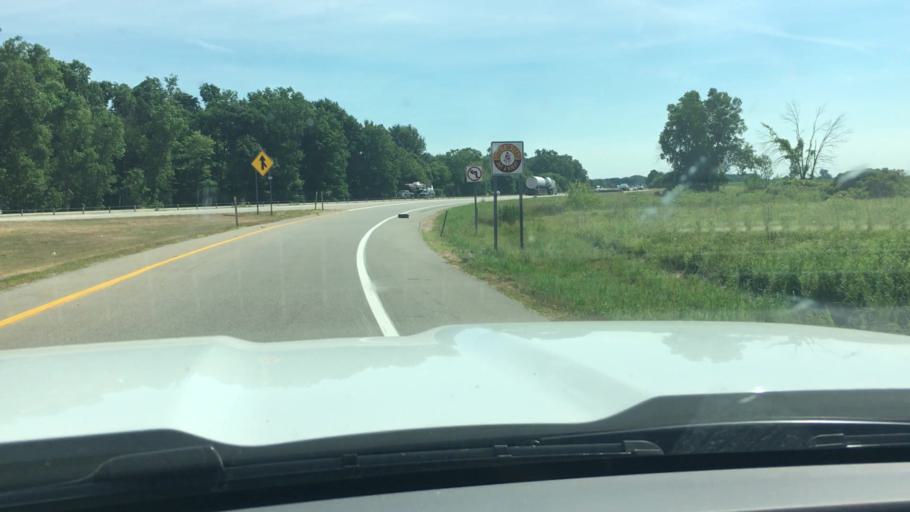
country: US
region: Michigan
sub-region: Ionia County
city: Saranac
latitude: 42.8786
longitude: -85.1565
